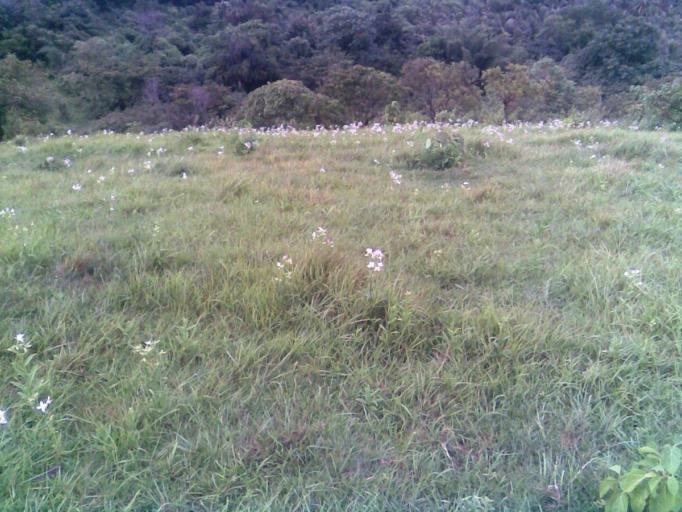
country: IN
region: Kerala
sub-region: Thrissur District
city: Avanoor
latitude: 10.6233
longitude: 76.1347
